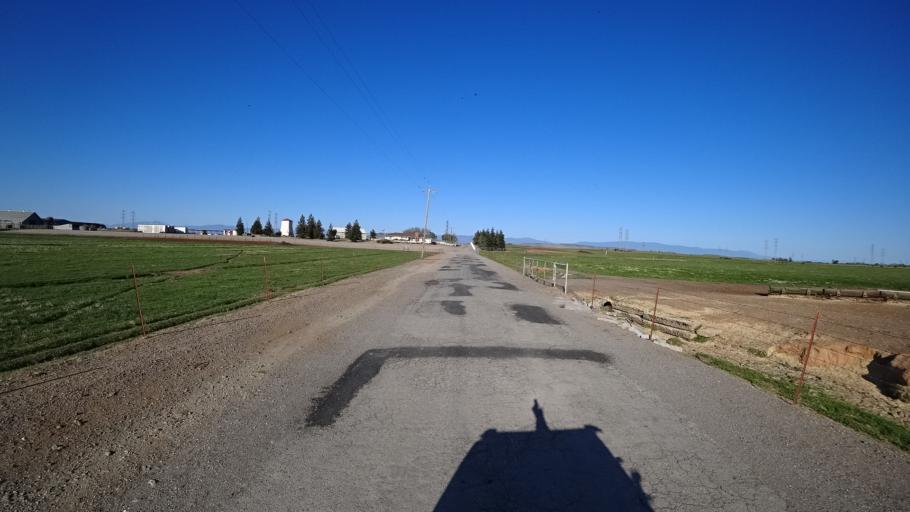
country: US
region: California
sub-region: Glenn County
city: Orland
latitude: 39.7589
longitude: -122.2600
